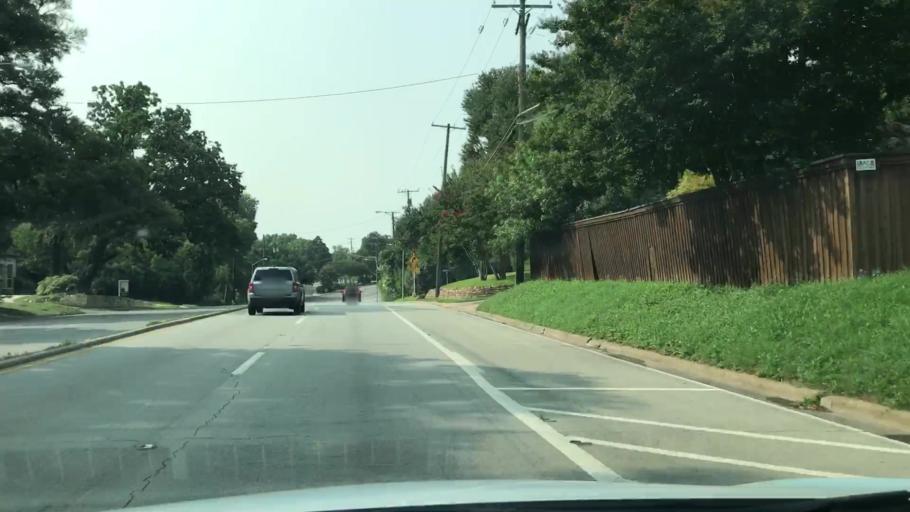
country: US
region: Texas
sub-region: Dallas County
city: Dallas
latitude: 32.7610
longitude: -96.8357
